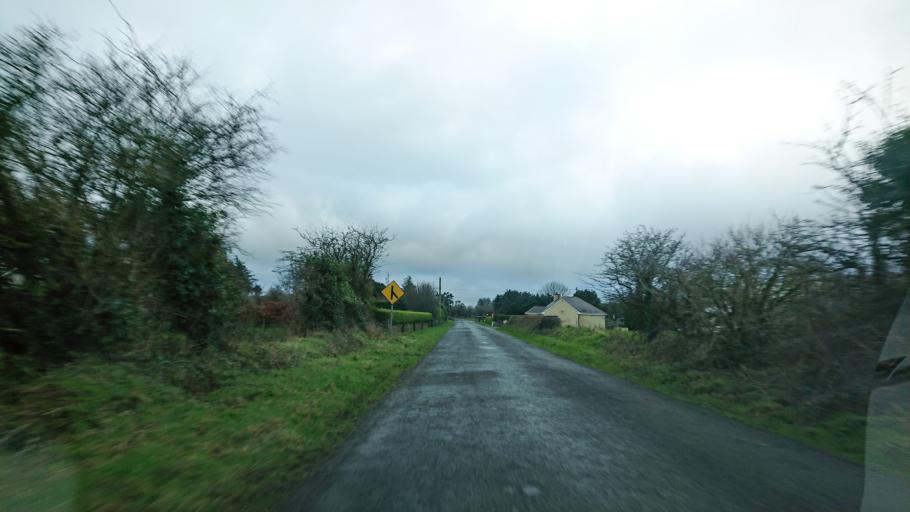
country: IE
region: Munster
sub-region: Waterford
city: Portlaw
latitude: 52.2574
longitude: -7.4043
